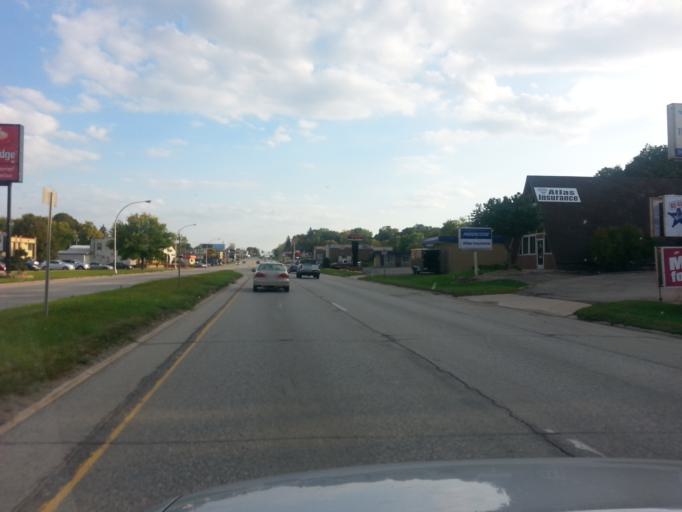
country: US
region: Minnesota
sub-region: Olmsted County
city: Rochester
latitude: 43.9955
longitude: -92.4632
